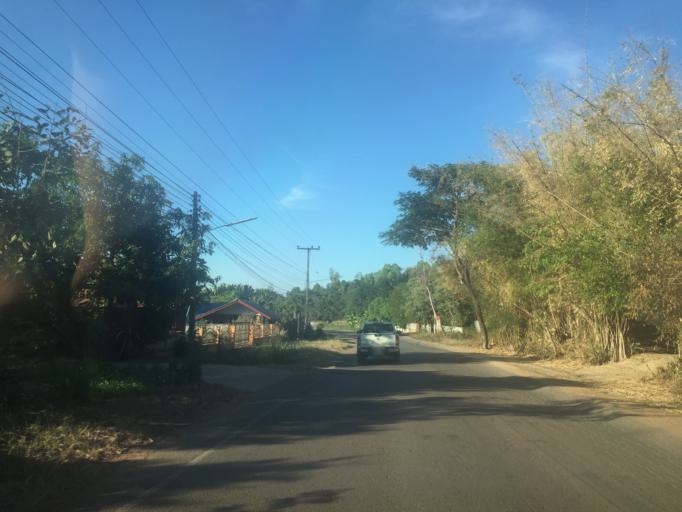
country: TH
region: Kalasin
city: Tha Khantho
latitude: 16.9695
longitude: 103.2661
